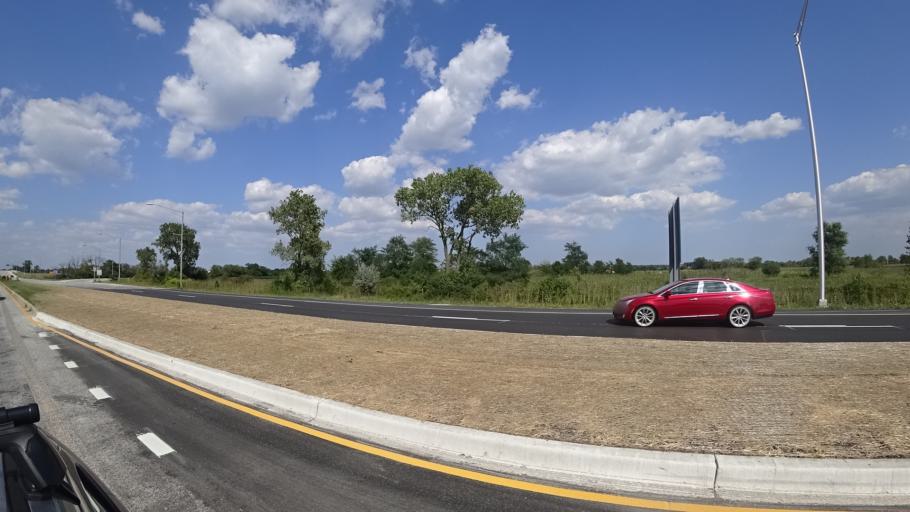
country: US
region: Illinois
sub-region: Will County
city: Frankfort Square
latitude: 41.5455
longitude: -87.7924
